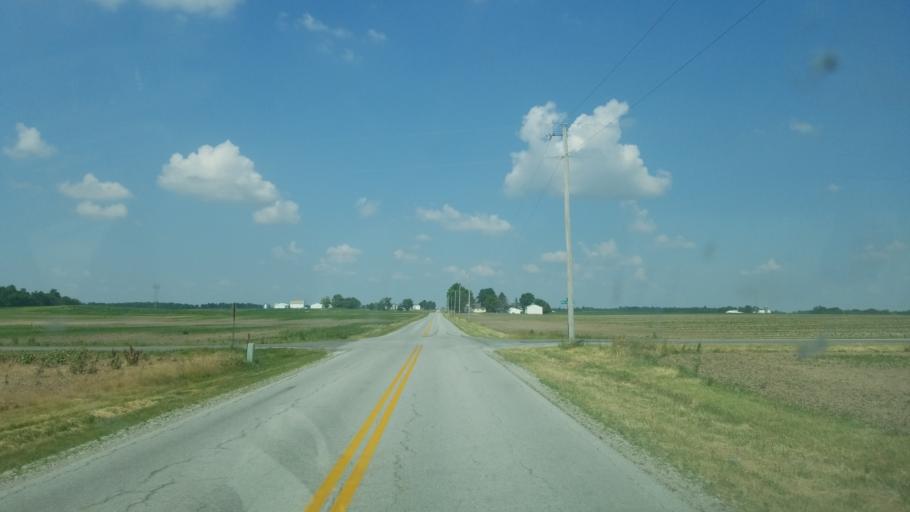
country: US
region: Ohio
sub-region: Auglaize County
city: Wapakoneta
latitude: 40.5707
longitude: -84.1069
